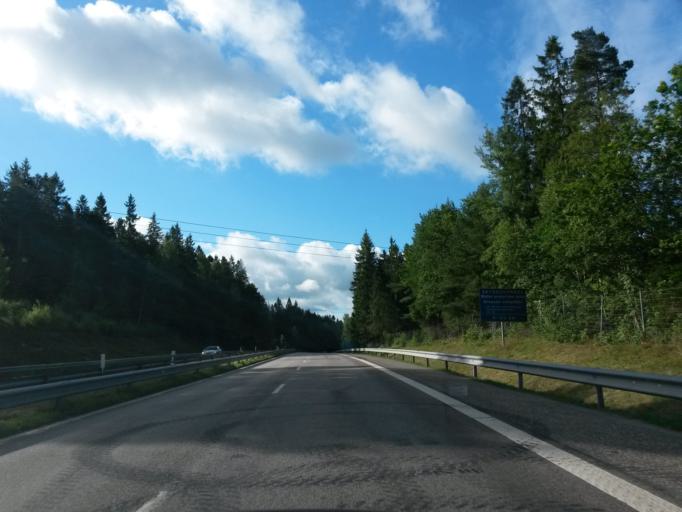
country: SE
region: Vaestra Goetaland
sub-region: Alingsas Kommun
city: Ingared
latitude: 57.8835
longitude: 12.4904
